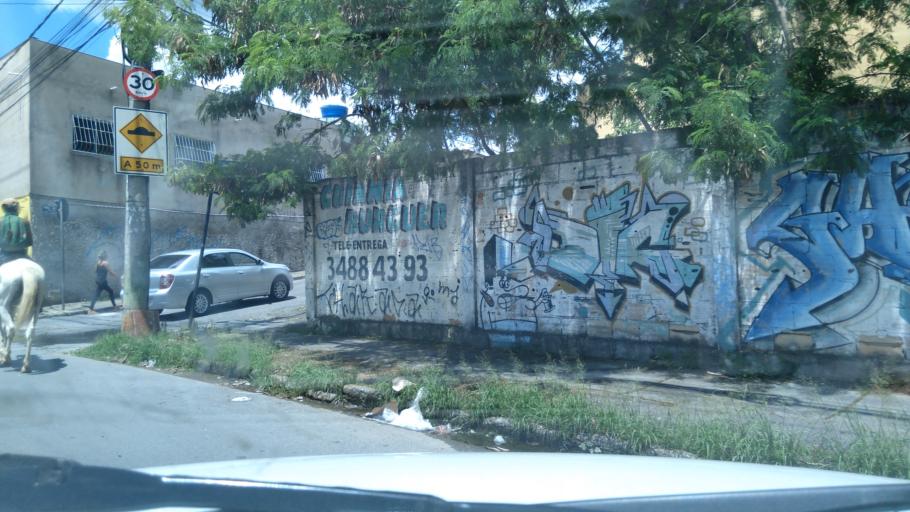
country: BR
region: Minas Gerais
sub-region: Belo Horizonte
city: Belo Horizonte
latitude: -19.8687
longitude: -43.8989
